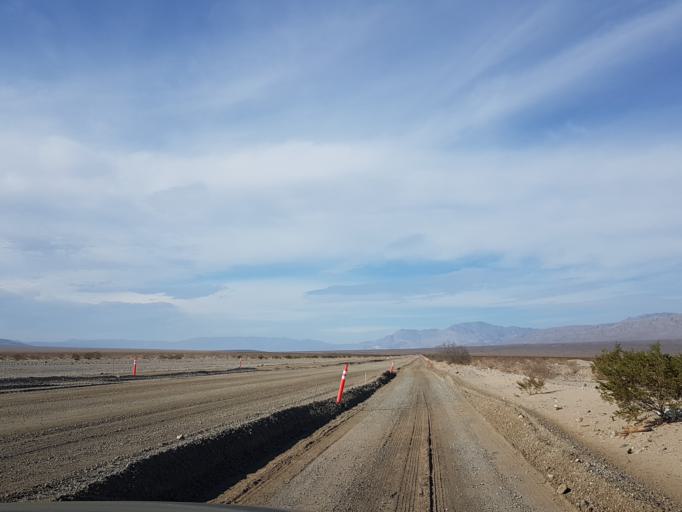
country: US
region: California
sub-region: San Bernardino County
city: Searles Valley
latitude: 36.1426
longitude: -117.2963
